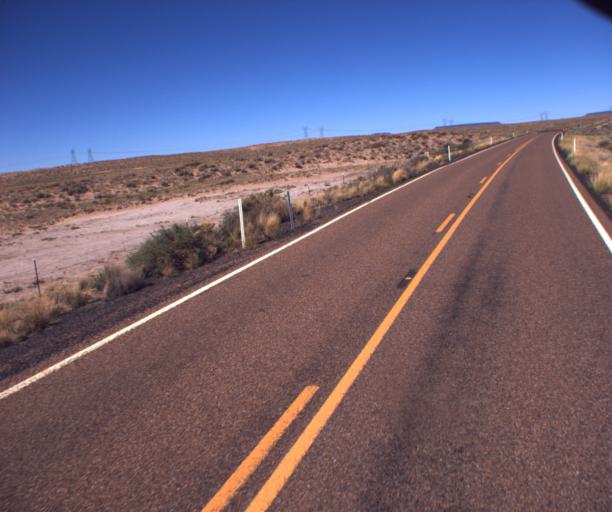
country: US
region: Arizona
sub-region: Navajo County
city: Holbrook
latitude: 35.1416
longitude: -110.0895
